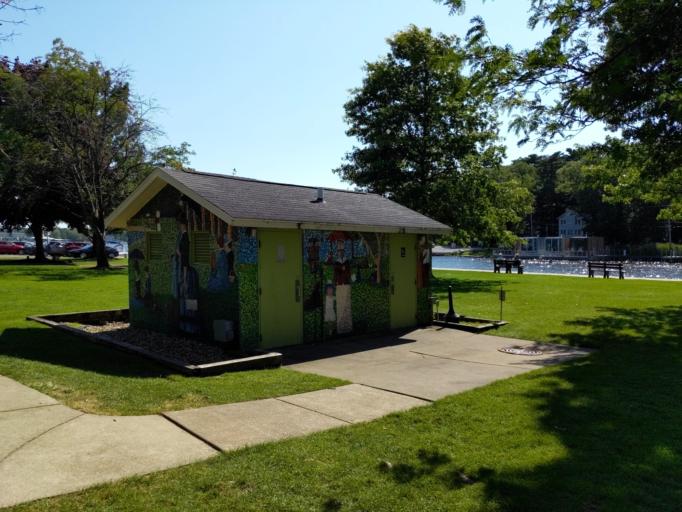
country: US
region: Michigan
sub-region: Allegan County
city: Douglas
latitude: 42.6582
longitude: -86.2055
